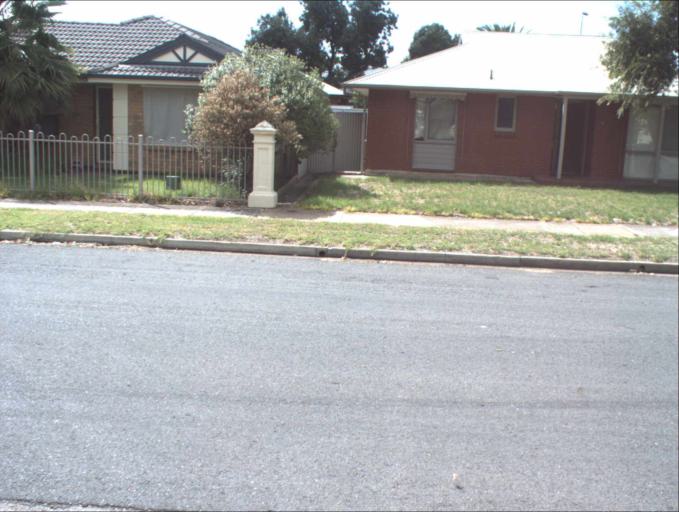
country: AU
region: South Australia
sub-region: Charles Sturt
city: Woodville North
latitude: -34.8673
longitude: 138.5621
